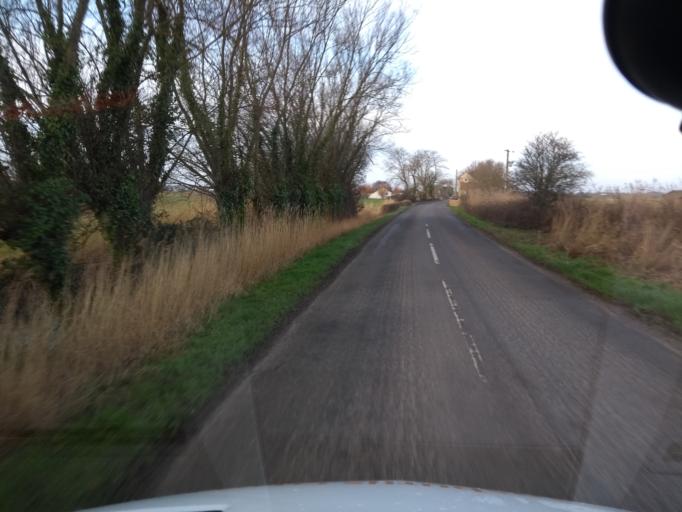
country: GB
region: England
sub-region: Somerset
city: Burnham-on-Sea
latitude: 51.2596
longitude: -2.9848
